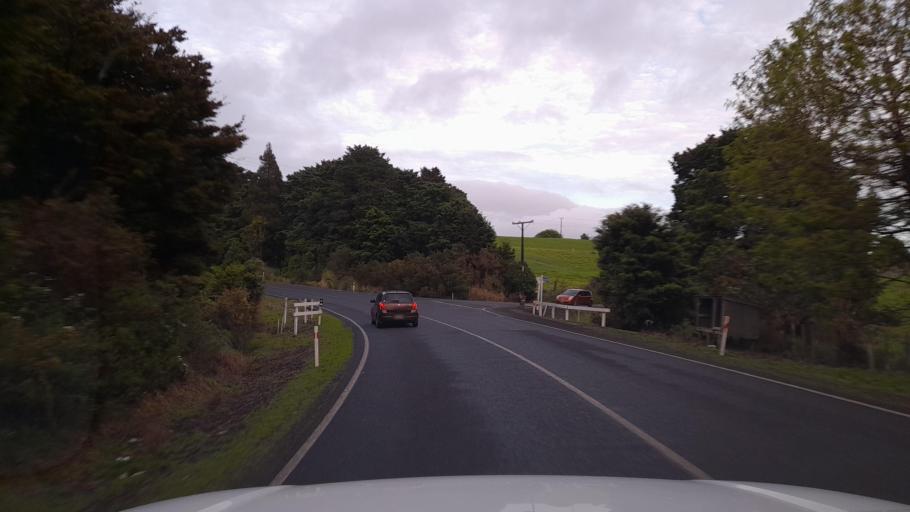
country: NZ
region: Northland
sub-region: Whangarei
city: Maungatapere
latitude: -35.7096
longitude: 174.0005
